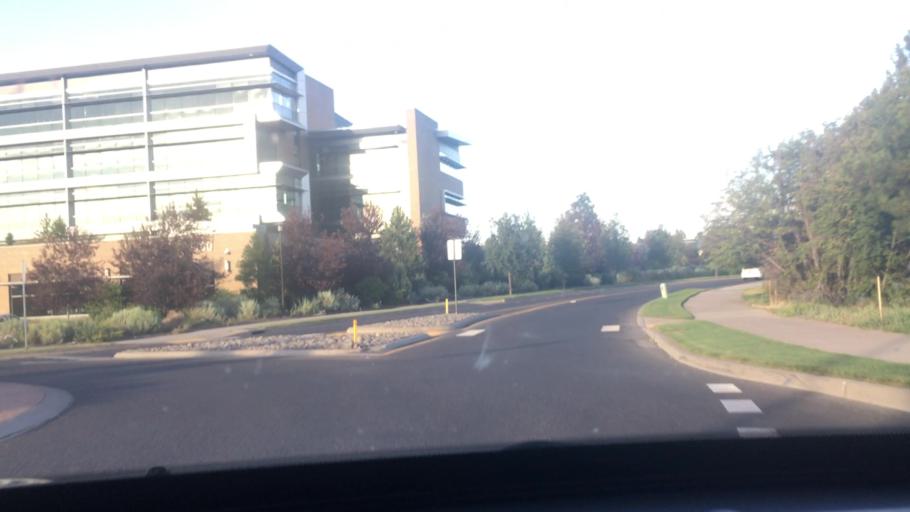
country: US
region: Oregon
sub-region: Deschutes County
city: Bend
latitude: 44.0460
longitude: -121.3098
